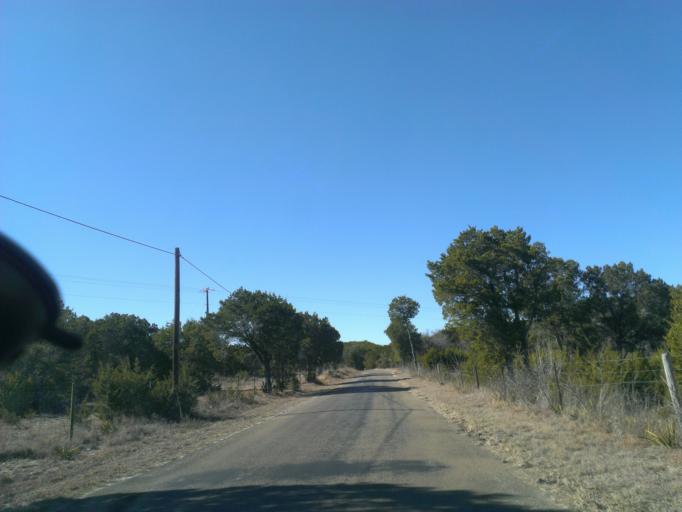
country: US
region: Texas
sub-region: Lampasas County
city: Lampasas
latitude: 30.9242
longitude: -98.1359
